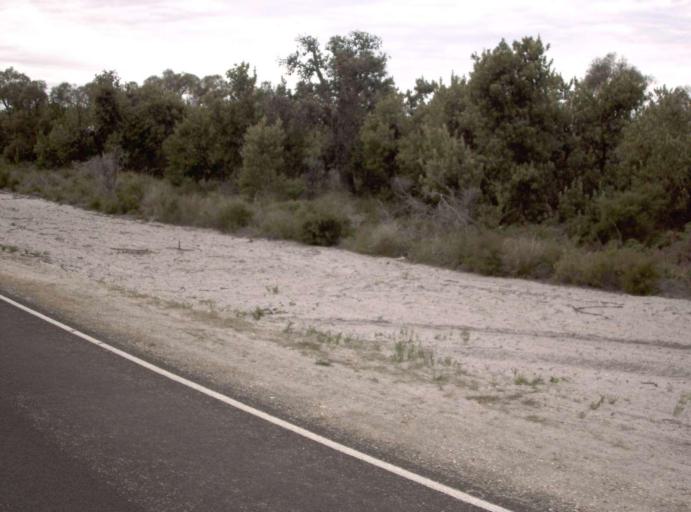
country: AU
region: Victoria
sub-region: Wellington
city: Sale
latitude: -38.1716
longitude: 147.3839
